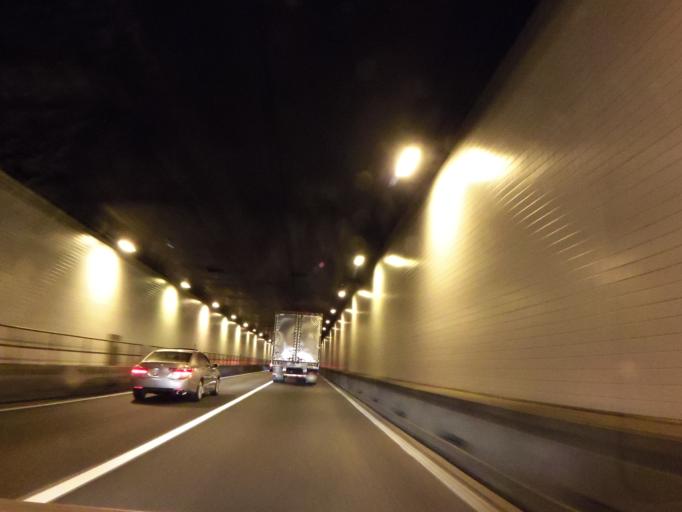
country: US
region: Virginia
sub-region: Bland County
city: Bland
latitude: 37.0385
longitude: -81.1308
